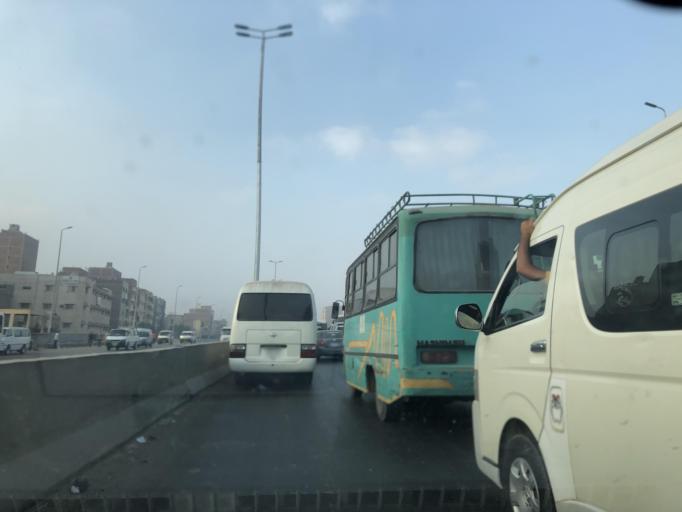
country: EG
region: Al Jizah
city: Awsim
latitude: 30.0727
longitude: 31.1759
